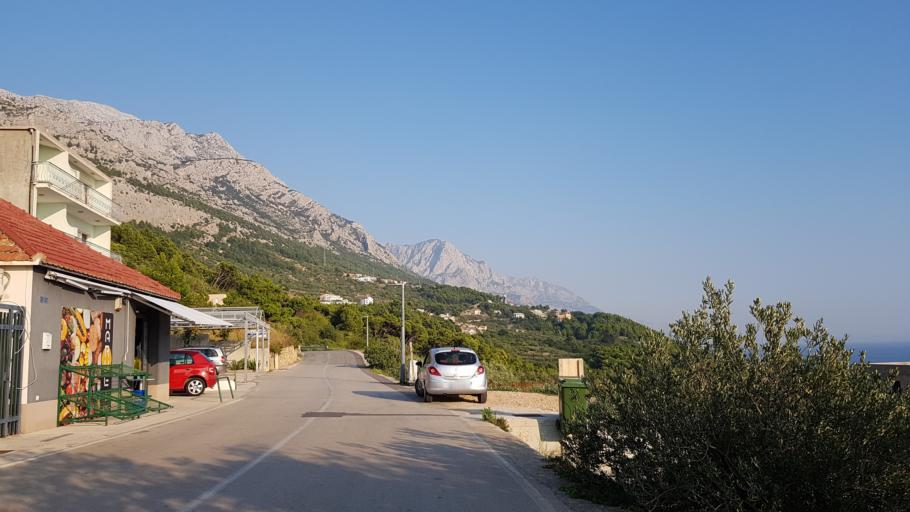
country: HR
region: Splitsko-Dalmatinska
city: Donja Brela
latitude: 43.3830
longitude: 16.9113
